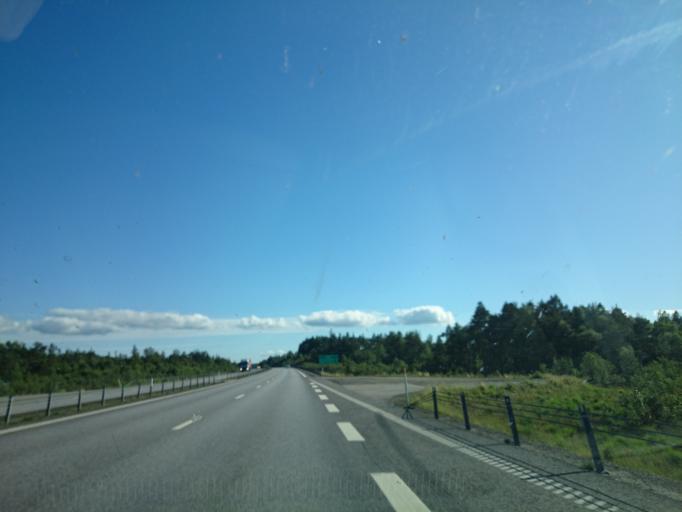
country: SE
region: Kronoberg
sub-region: Markaryds Kommun
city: Markaryd
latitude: 56.3551
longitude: 13.4708
